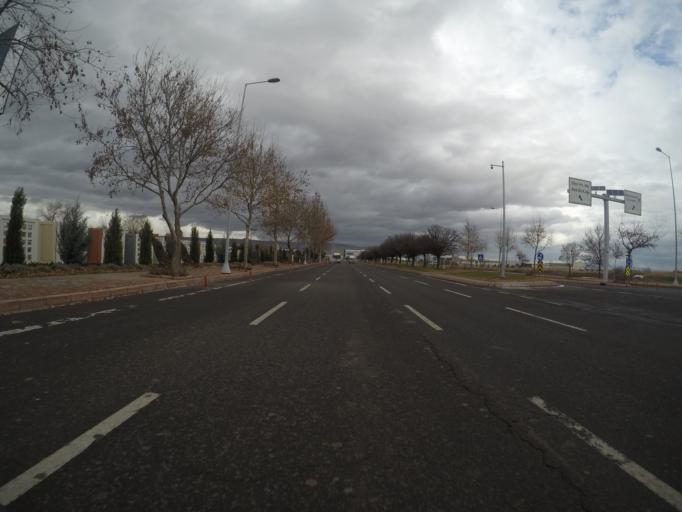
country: TR
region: Kayseri
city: Kayseri
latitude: 38.7619
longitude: 35.4818
